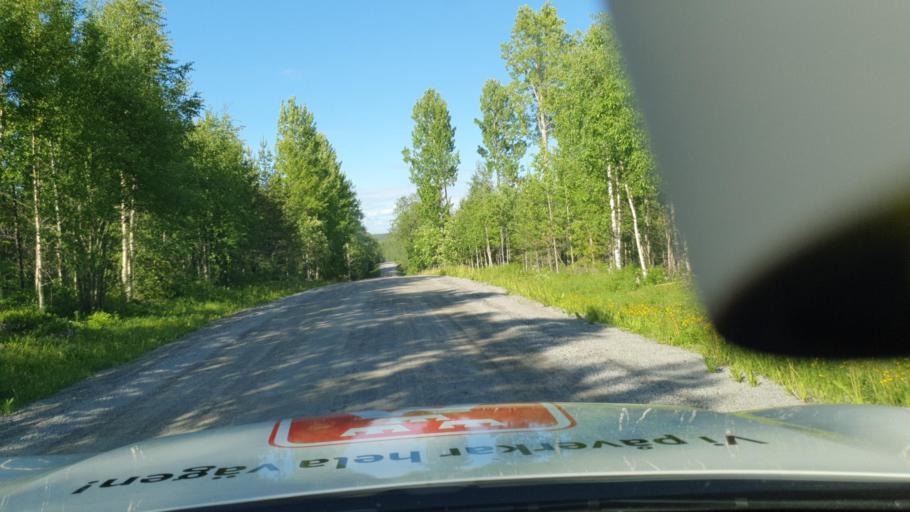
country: SE
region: Vaesterbotten
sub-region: Vannas Kommun
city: Vaennaes
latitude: 63.7993
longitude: 19.6323
